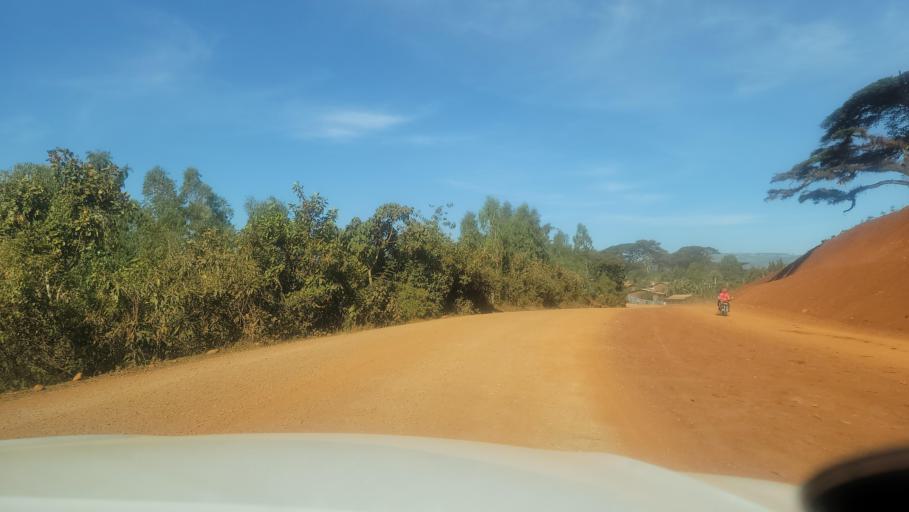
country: ET
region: Oromiya
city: Agaro
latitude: 7.8165
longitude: 36.5215
